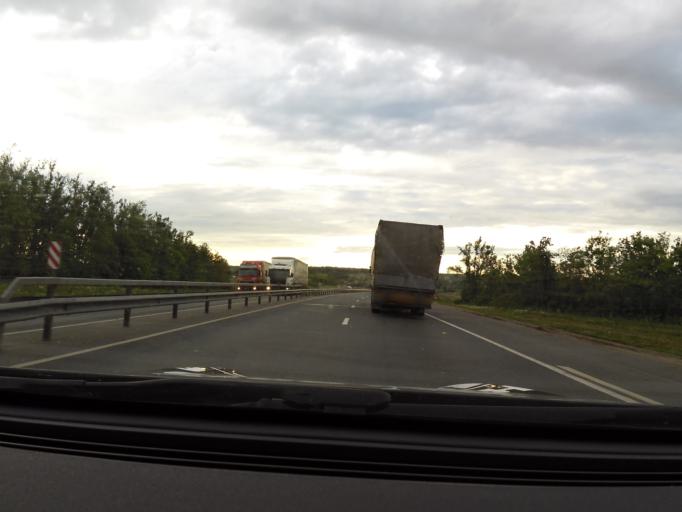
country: RU
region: Chuvashia
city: Tsivil'sk
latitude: 55.9240
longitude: 47.4015
